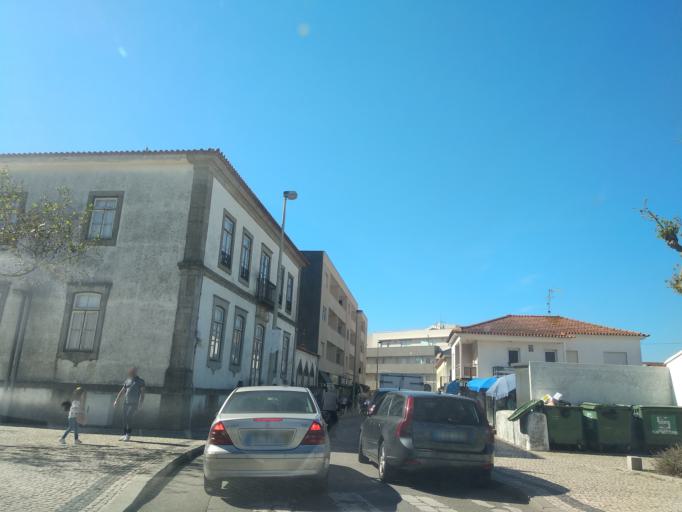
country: PT
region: Braga
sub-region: Esposende
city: Apulia
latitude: 41.4849
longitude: -8.7777
